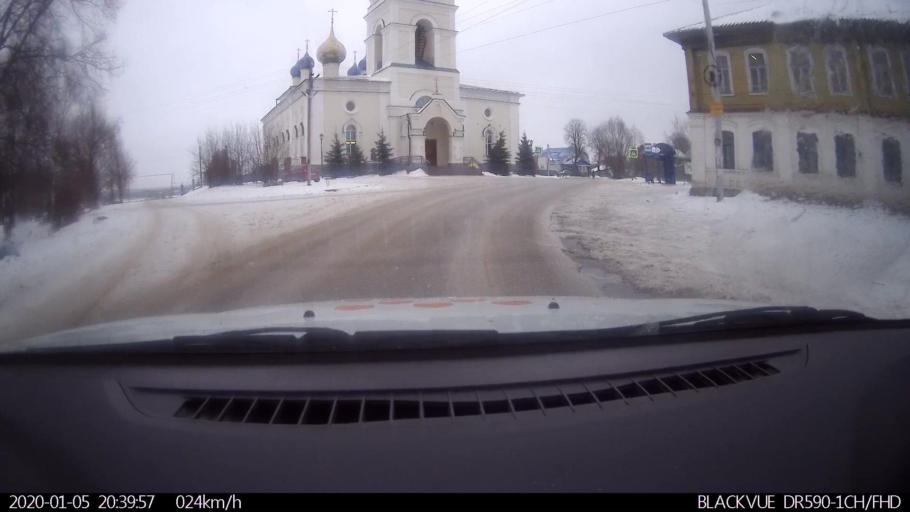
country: RU
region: Nizjnij Novgorod
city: Lukino
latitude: 56.4122
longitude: 43.7282
